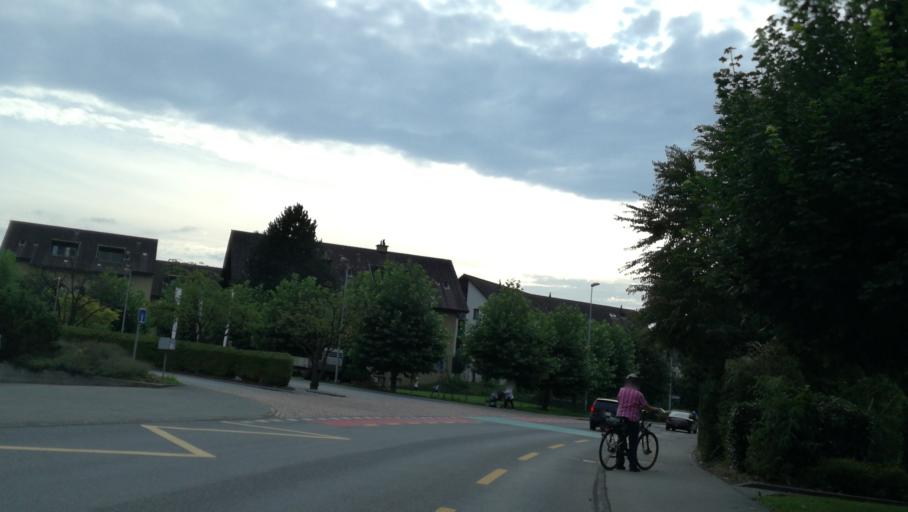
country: CH
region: Lucerne
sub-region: Lucerne-Land District
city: Ebikon
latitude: 47.0841
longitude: 8.3494
